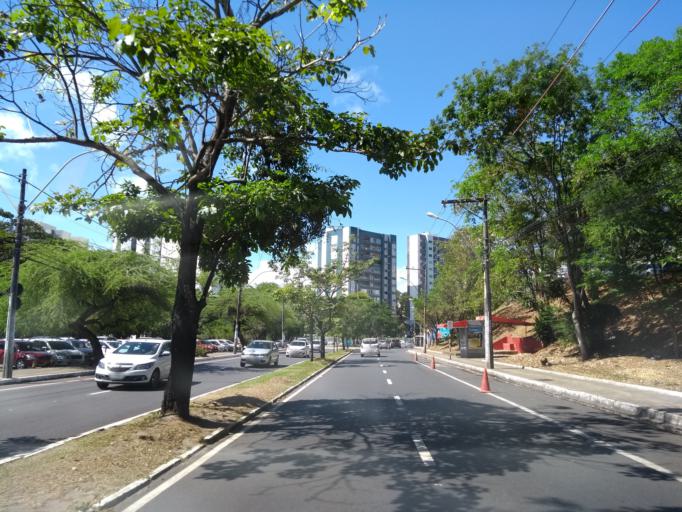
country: BR
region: Bahia
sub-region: Salvador
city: Salvador
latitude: -12.9952
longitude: -38.4643
